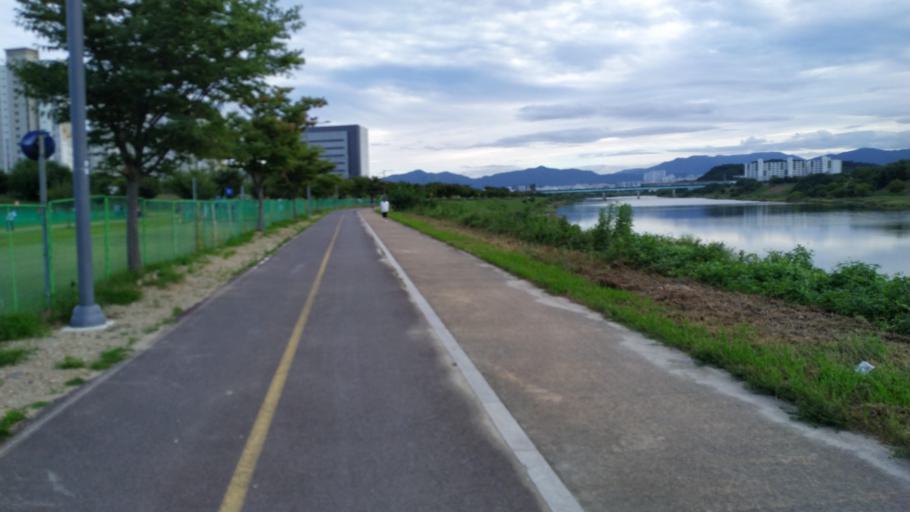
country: KR
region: Daegu
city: Daegu
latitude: 35.9271
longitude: 128.6318
